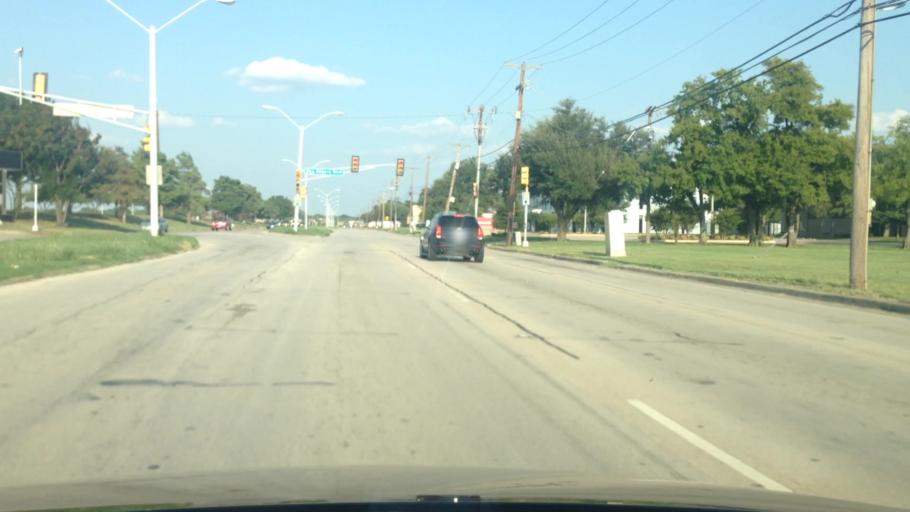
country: US
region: Texas
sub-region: Tarrant County
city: Everman
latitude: 32.6274
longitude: -97.3136
